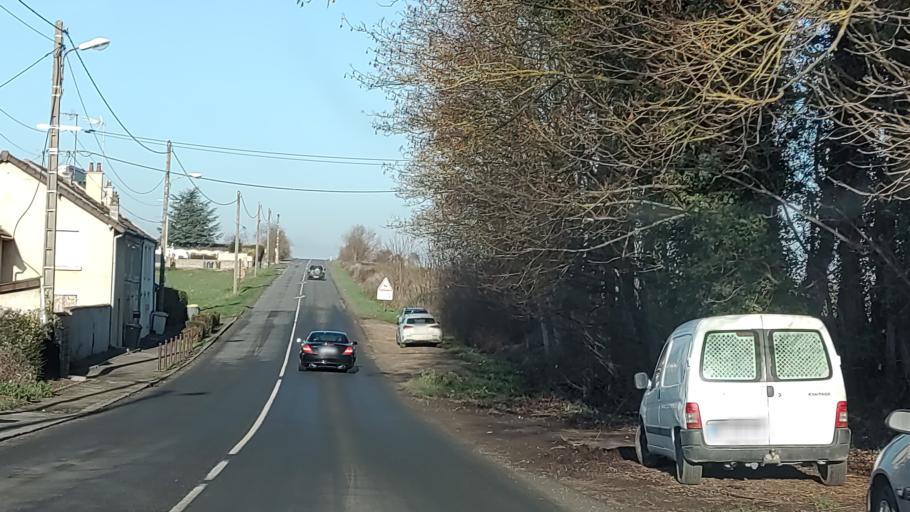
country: FR
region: Ile-de-France
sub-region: Departement de Seine-et-Marne
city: Claye-Souilly
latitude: 48.9492
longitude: 2.6921
